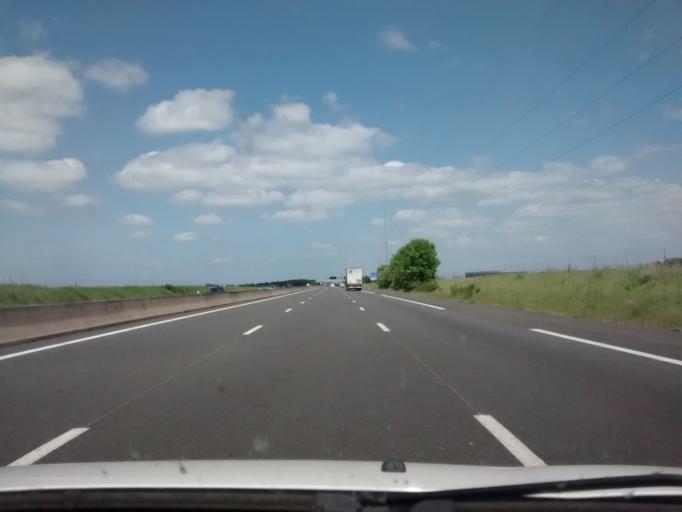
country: FR
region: Centre
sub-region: Departement d'Eure-et-Loir
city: Dammarie
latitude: 48.3473
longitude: 1.4169
